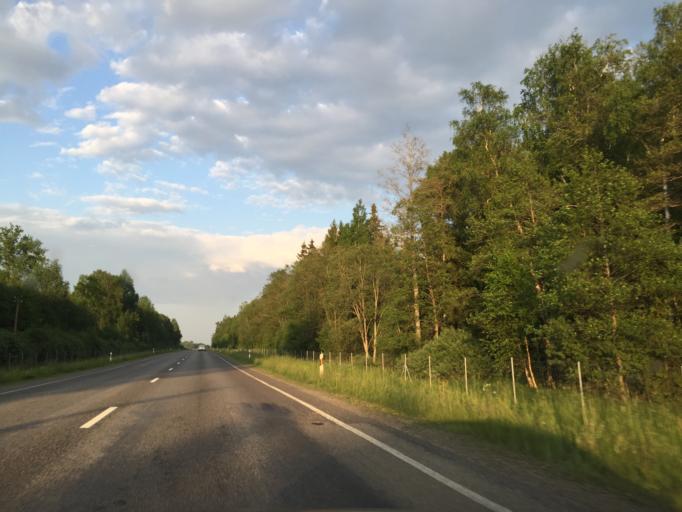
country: LT
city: Kursenai
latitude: 55.9994
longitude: 22.8256
